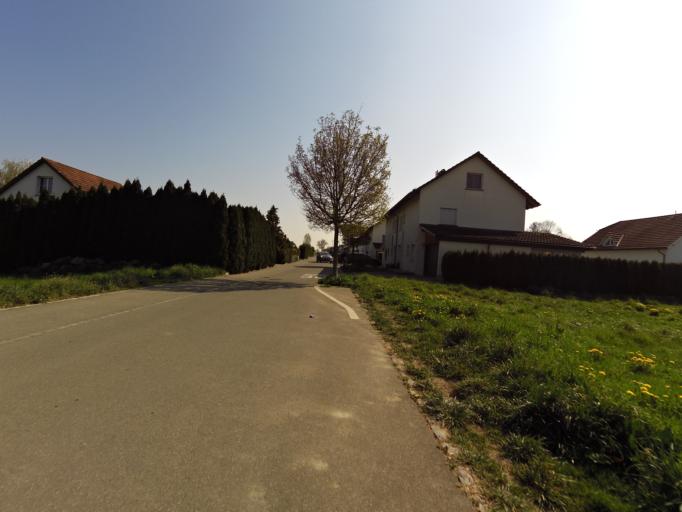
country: CH
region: Thurgau
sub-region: Frauenfeld District
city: Gachnang
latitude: 47.5504
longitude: 8.8619
